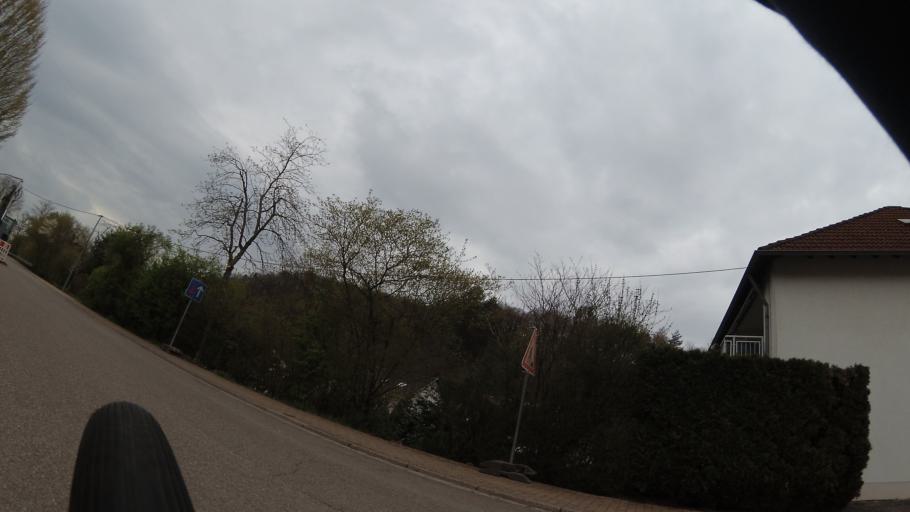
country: DE
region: Saarland
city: Merzig
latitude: 49.4617
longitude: 6.6450
